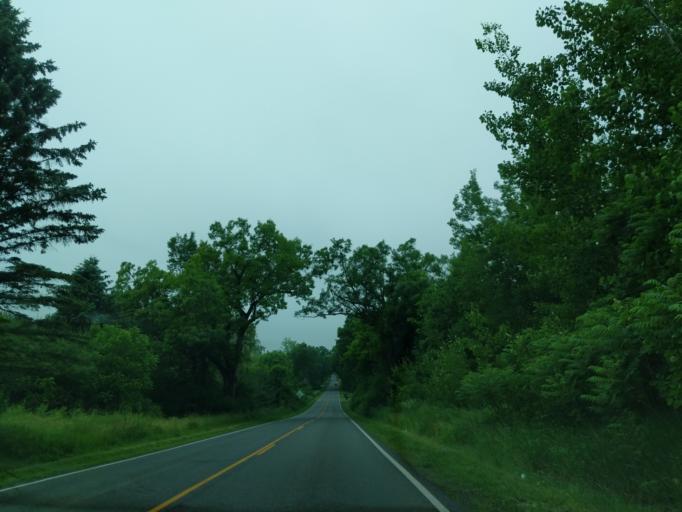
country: US
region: Michigan
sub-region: Jackson County
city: Spring Arbor
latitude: 42.2134
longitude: -84.5409
